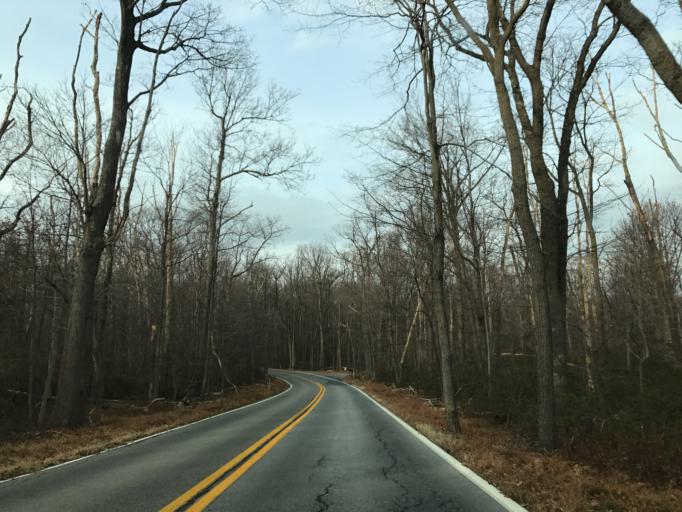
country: US
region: Maryland
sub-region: Frederick County
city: Braddock Heights
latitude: 39.4773
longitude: -77.4925
